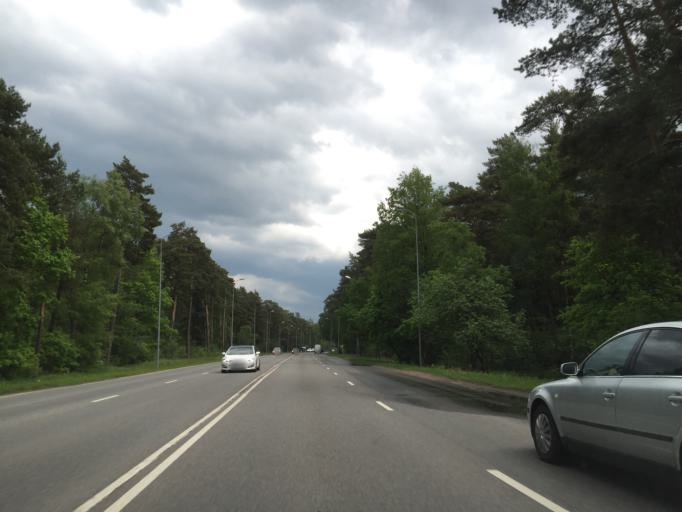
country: LT
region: Klaipedos apskritis
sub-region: Klaipeda
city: Klaipeda
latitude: 55.7333
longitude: 21.1125
